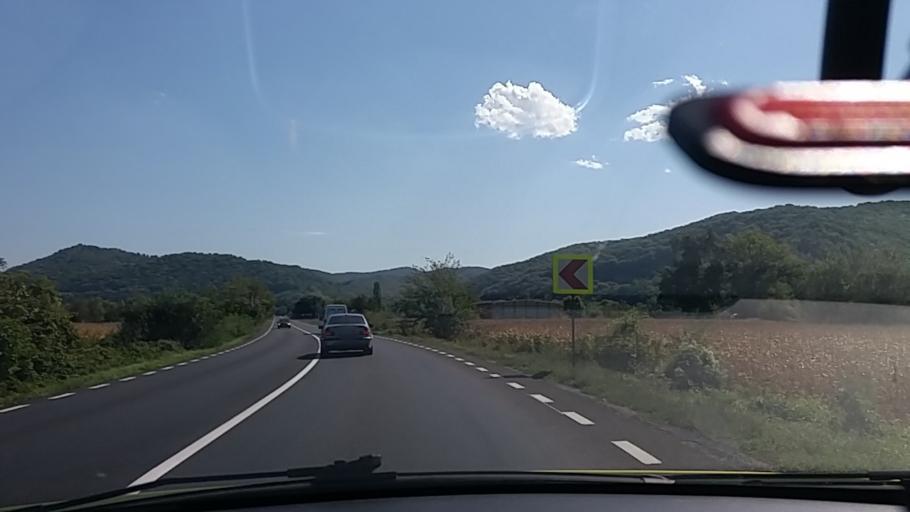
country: RO
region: Hunedoara
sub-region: Comuna Ilia
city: Ilia
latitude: 45.9282
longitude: 22.6594
